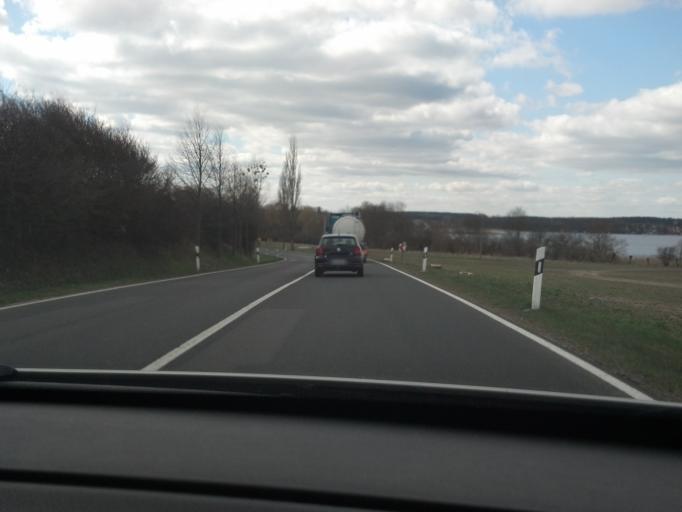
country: DE
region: Mecklenburg-Vorpommern
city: Wesenberg
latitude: 53.2808
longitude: 12.9921
